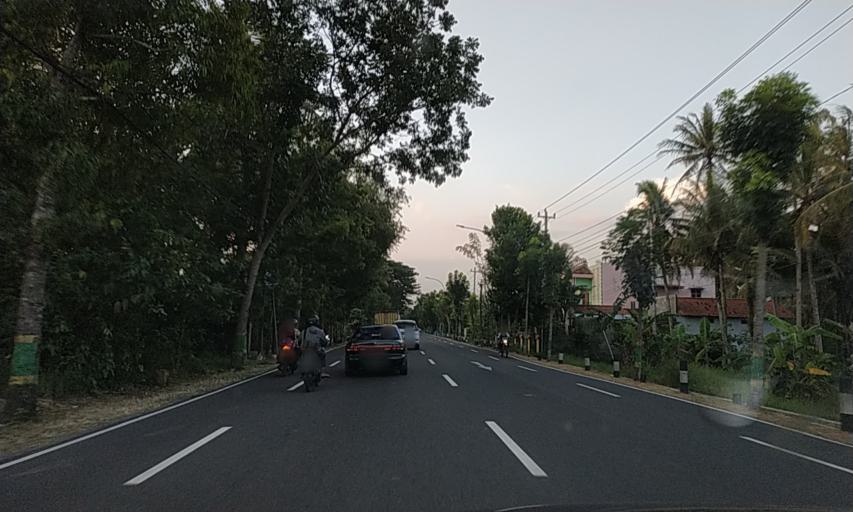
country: ID
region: Daerah Istimewa Yogyakarta
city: Srandakan
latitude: -7.8874
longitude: 110.1304
